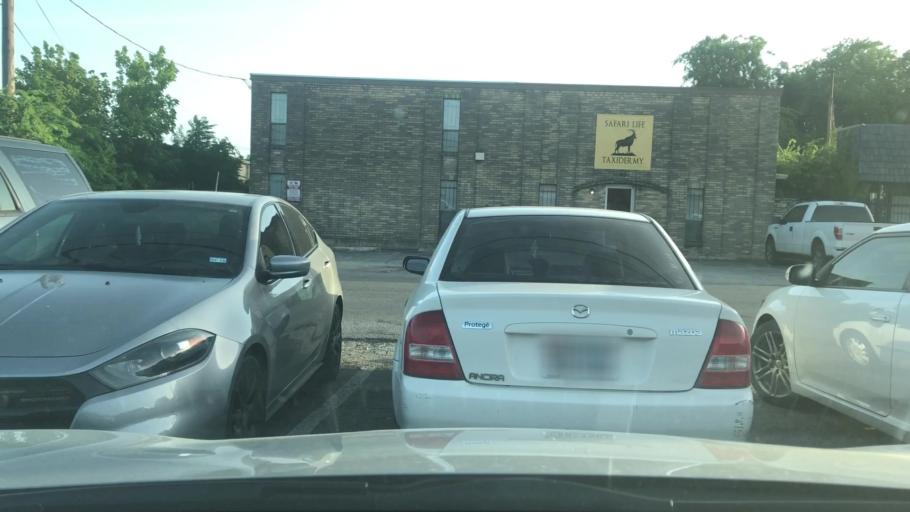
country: US
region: Texas
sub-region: Bexar County
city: Olmos Park
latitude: 29.4936
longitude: -98.5000
